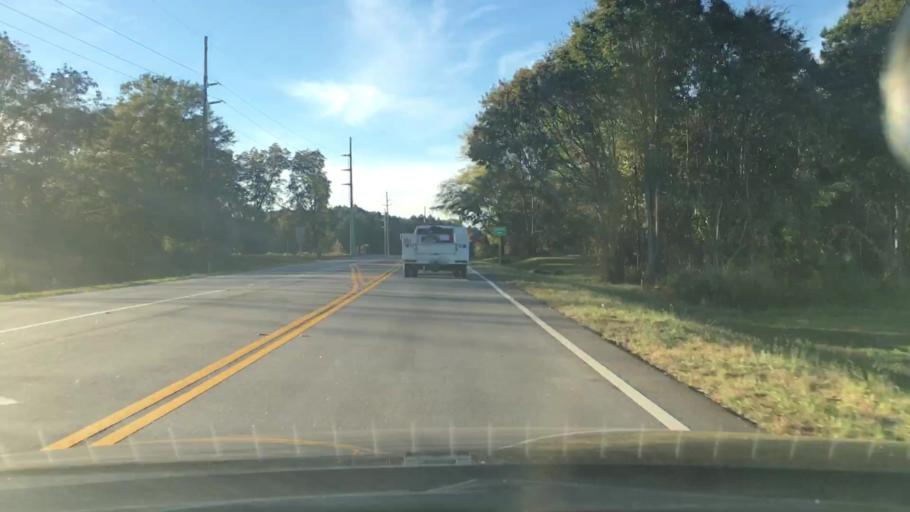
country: US
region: Georgia
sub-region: Coweta County
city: Senoia
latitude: 33.2984
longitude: -84.5901
